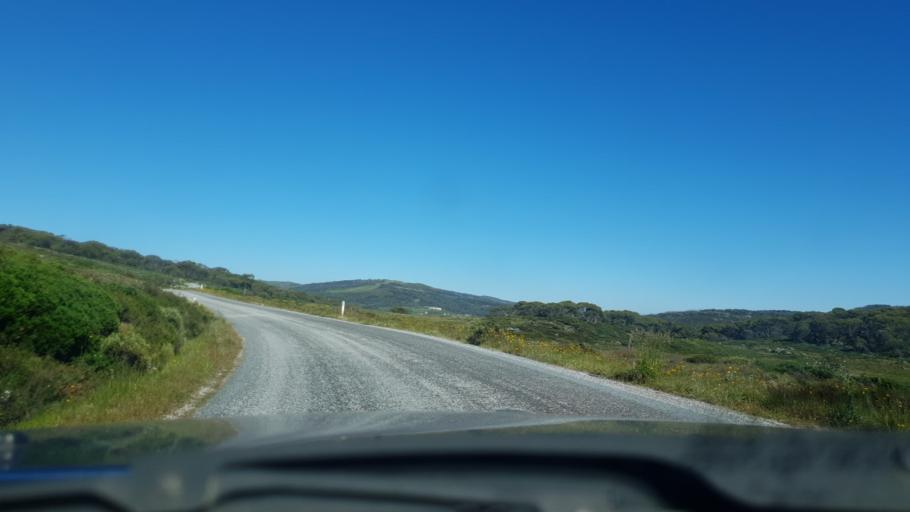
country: AU
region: Victoria
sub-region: Alpine
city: Mount Beauty
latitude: -36.8836
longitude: 147.3149
